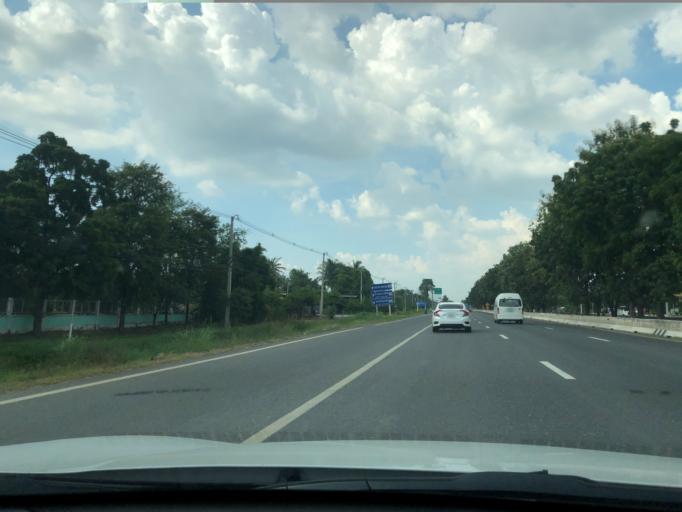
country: TH
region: Nakhon Sawan
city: Krok Phra
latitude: 15.5838
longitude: 100.1241
